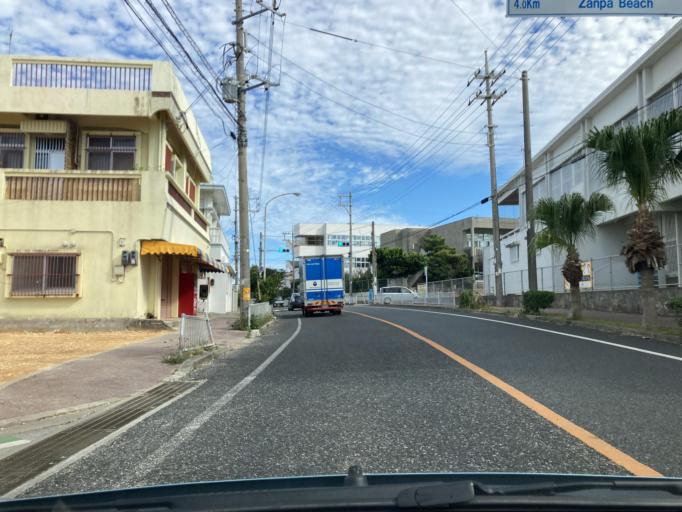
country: JP
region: Okinawa
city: Ishikawa
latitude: 26.4069
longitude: 127.7316
